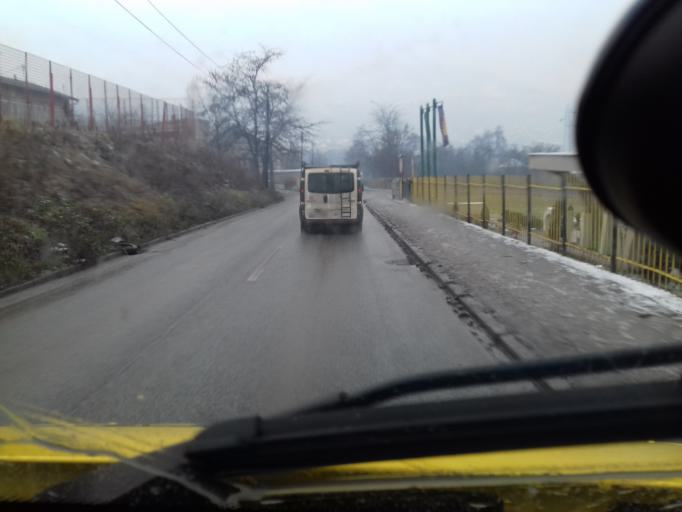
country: BA
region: Federation of Bosnia and Herzegovina
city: Zenica
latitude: 44.2283
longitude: 17.8900
